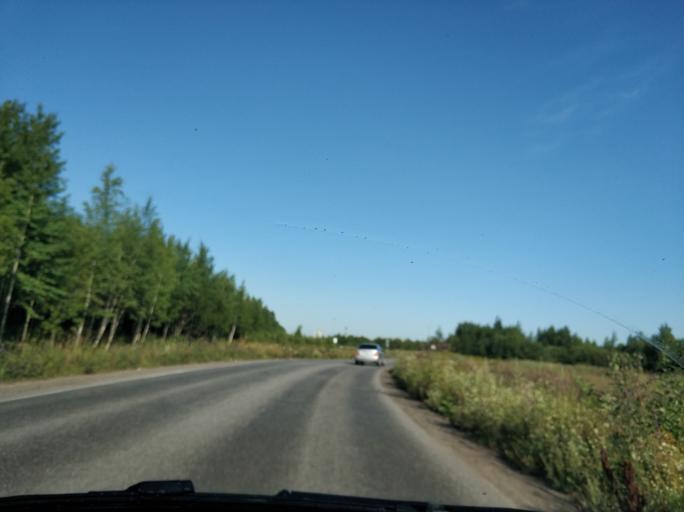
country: RU
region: St.-Petersburg
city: Grazhdanka
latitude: 60.0492
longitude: 30.4046
